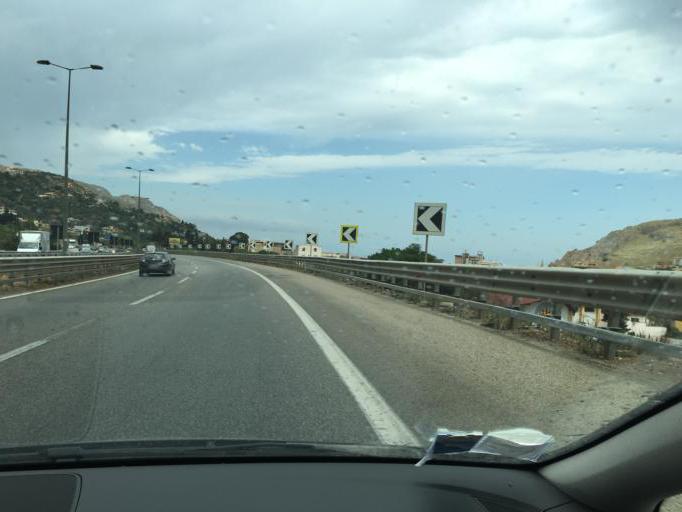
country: IT
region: Sicily
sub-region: Palermo
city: Isola delle Femmine
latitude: 38.1857
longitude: 13.2888
